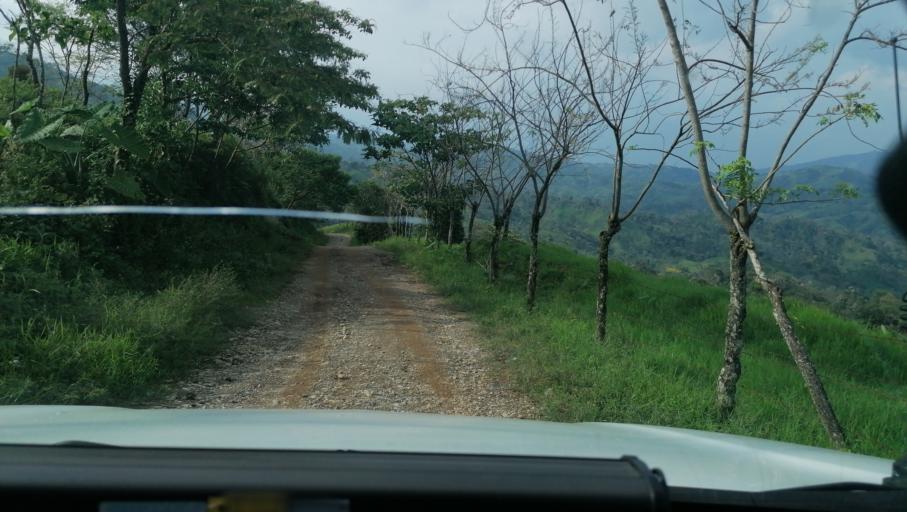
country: MX
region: Chiapas
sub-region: Tapilula
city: San Francisco Jacona
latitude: 17.3230
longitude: -93.0993
